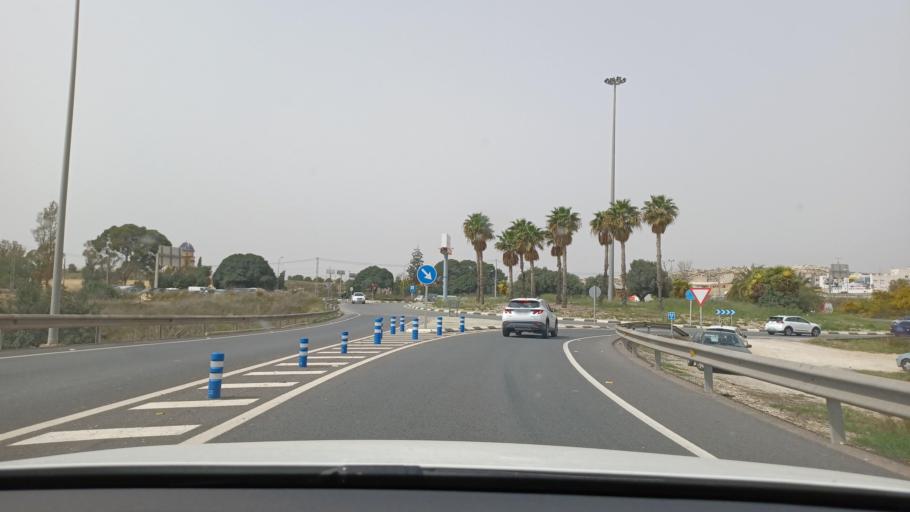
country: ES
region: Valencia
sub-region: Provincia de Alicante
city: Alicante
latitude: 38.3832
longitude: -0.4879
